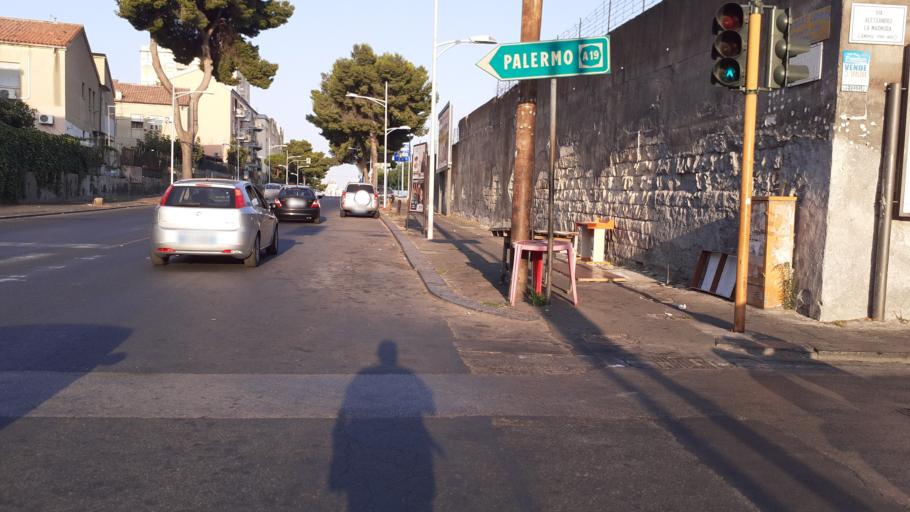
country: IT
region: Sicily
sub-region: Catania
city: Catania
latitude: 37.5016
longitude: 15.0628
